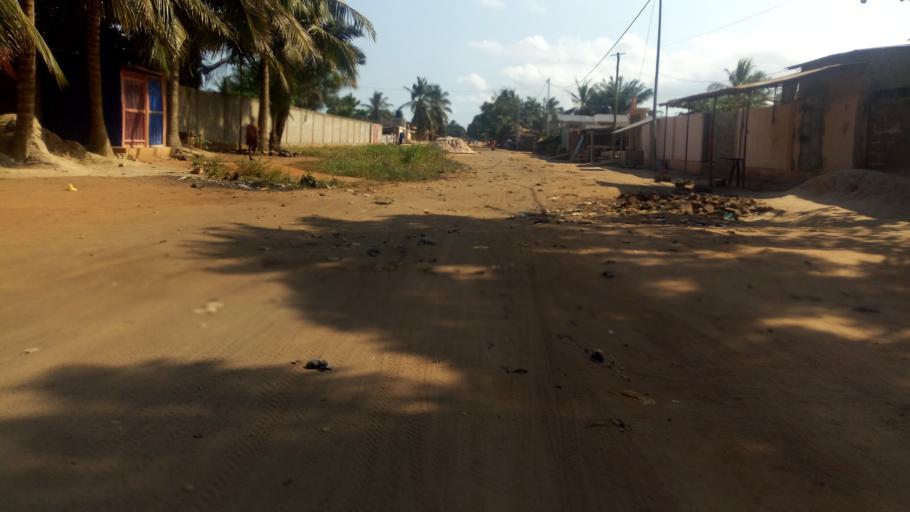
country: TG
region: Maritime
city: Lome
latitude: 6.2292
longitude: 1.1822
